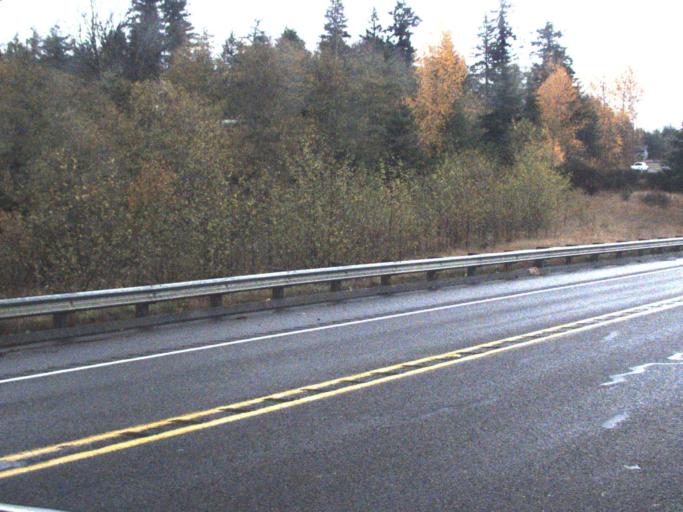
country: US
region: Washington
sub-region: Snohomish County
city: Fobes Hill
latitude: 47.9539
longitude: -122.1127
